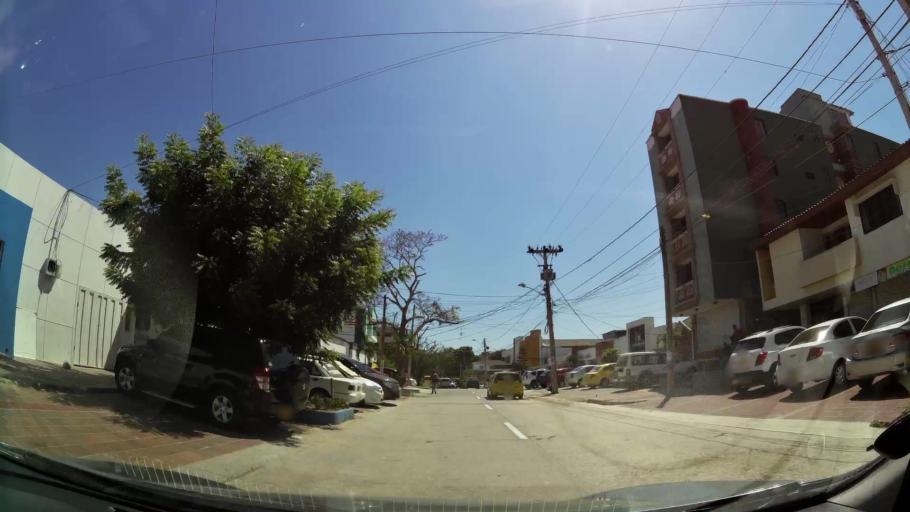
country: CO
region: Atlantico
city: Barranquilla
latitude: 10.9981
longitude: -74.8090
